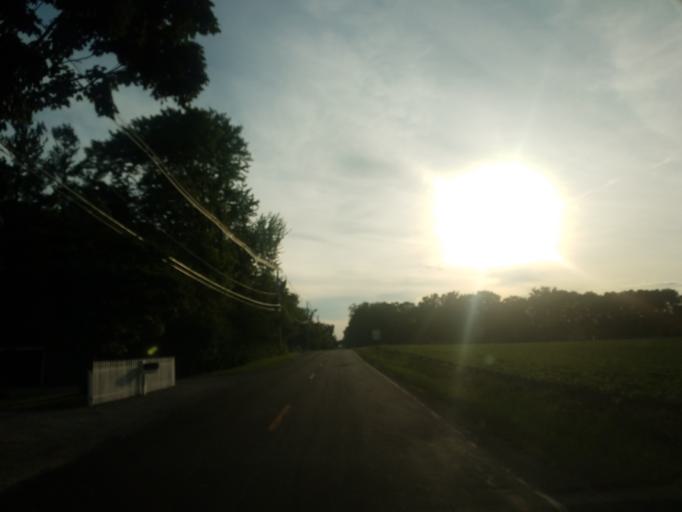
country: US
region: Illinois
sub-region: McLean County
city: Bloomington
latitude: 40.4440
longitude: -88.9813
